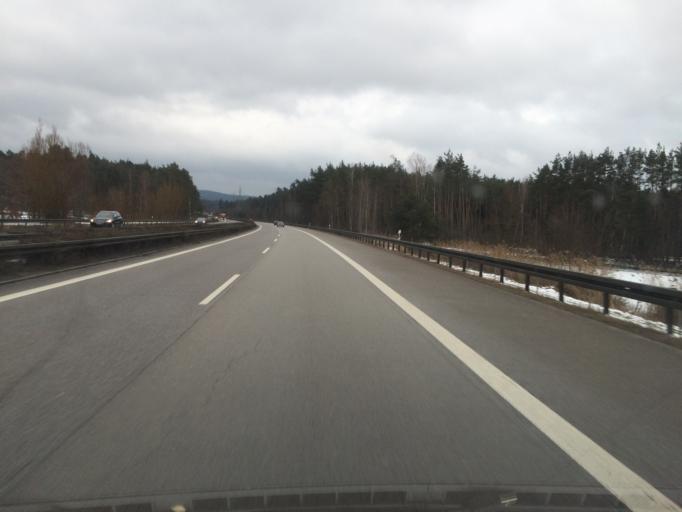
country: DE
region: Bavaria
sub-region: Upper Palatinate
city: Teublitz
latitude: 49.2574
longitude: 12.1232
